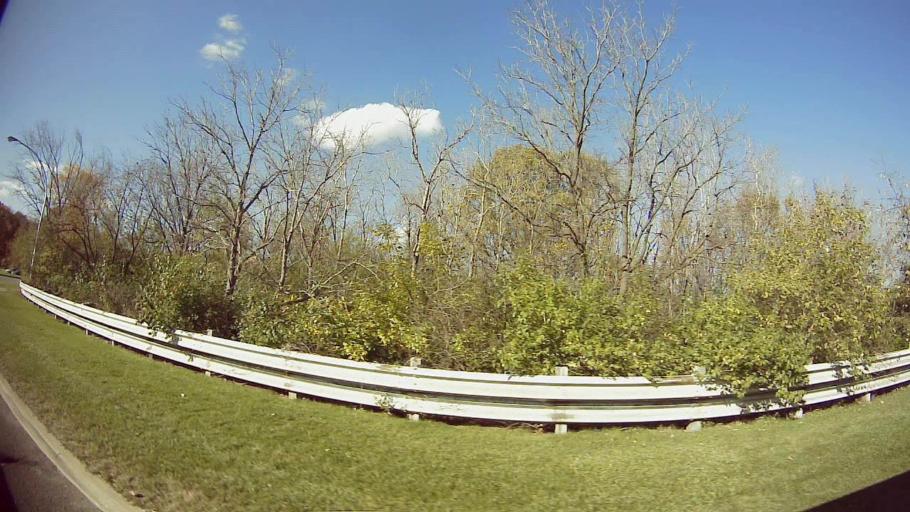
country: US
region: Michigan
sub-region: Wayne County
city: Dearborn
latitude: 42.3094
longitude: -83.2249
